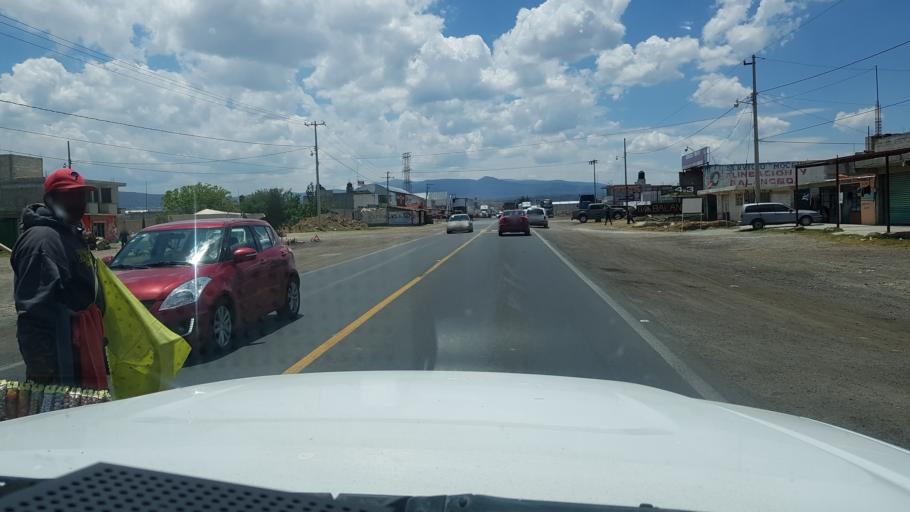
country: MX
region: Hidalgo
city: Calpulalpan
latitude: 19.5991
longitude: -98.5694
